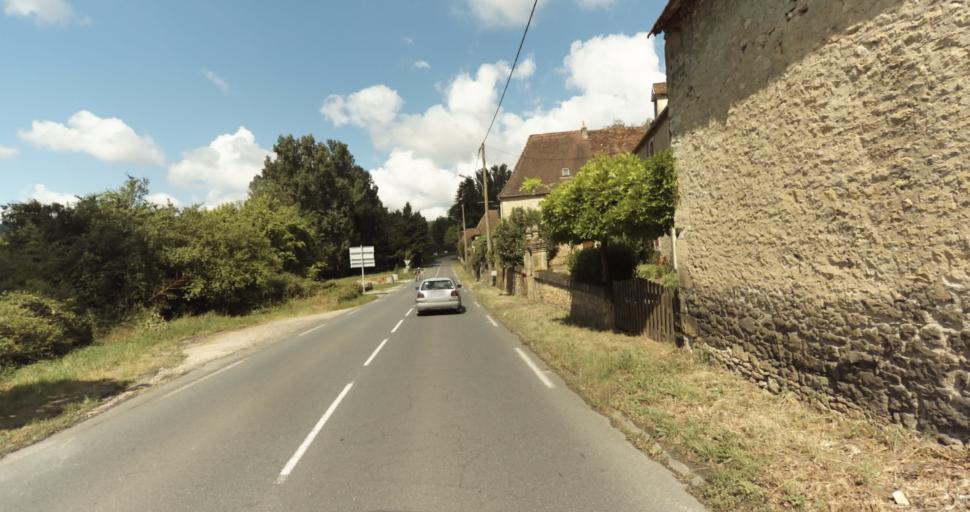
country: FR
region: Aquitaine
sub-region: Departement de la Dordogne
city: Le Bugue
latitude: 44.8563
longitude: 0.9081
